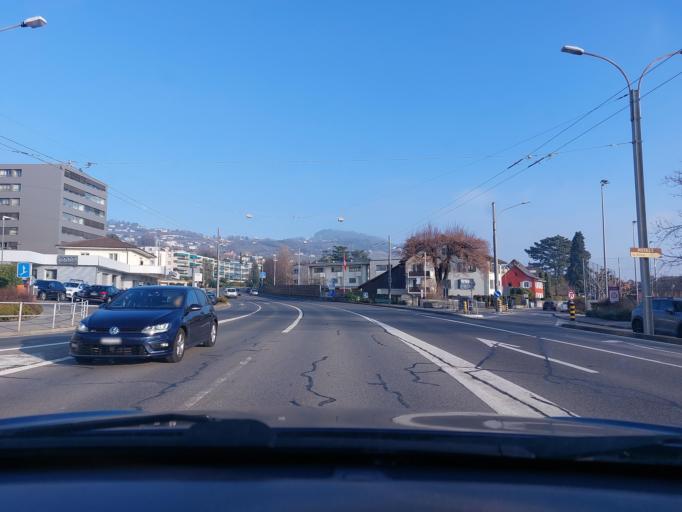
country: CH
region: Vaud
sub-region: Lavaux-Oron District
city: Lutry
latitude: 46.5040
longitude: 6.6805
